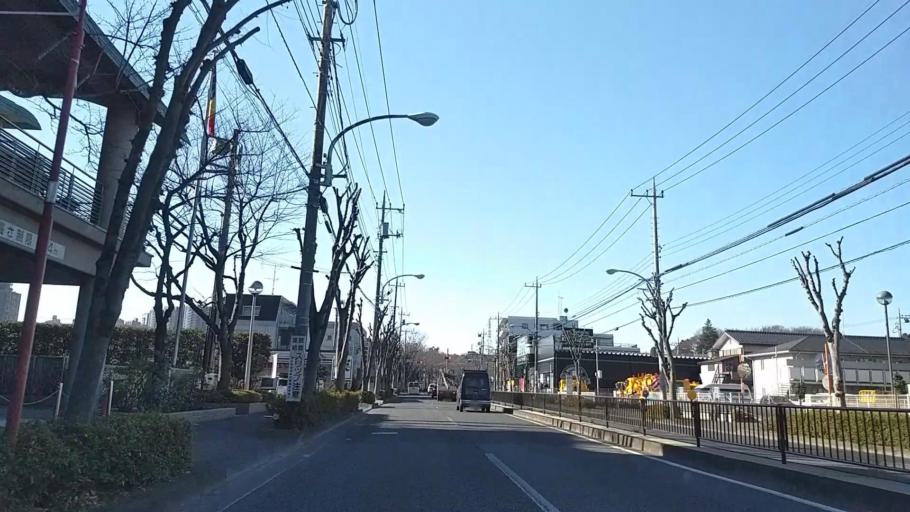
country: JP
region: Tokyo
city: Hino
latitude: 35.6253
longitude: 139.3789
